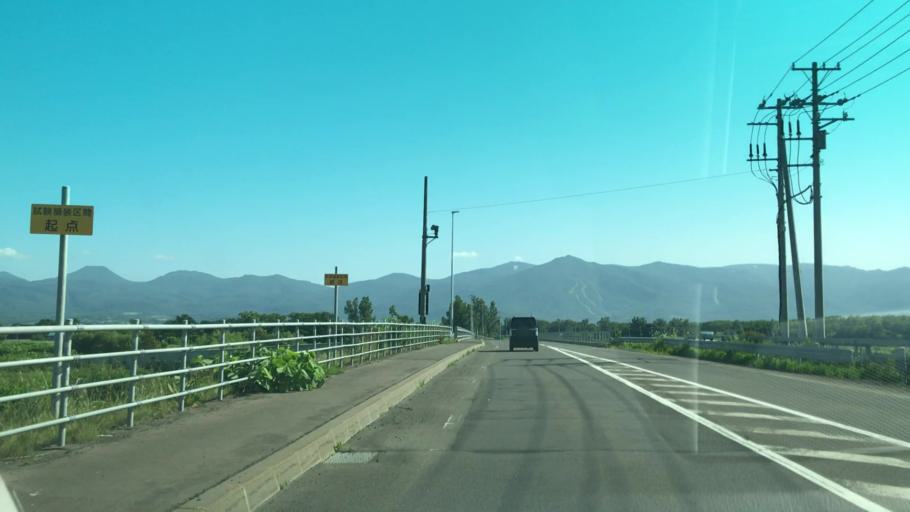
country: JP
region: Hokkaido
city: Iwanai
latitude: 43.0232
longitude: 140.5484
